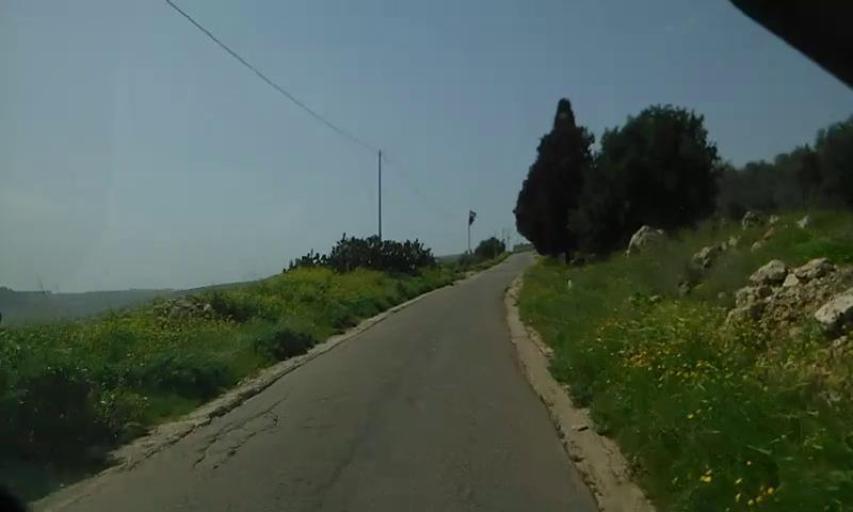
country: PS
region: West Bank
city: `Anin
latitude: 32.4981
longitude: 35.1775
